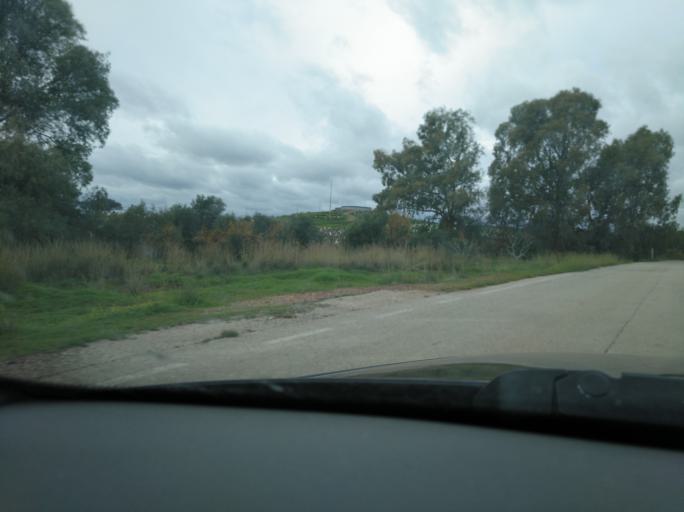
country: PT
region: Faro
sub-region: Vila Real de Santo Antonio
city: Monte Gordo
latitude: 37.2011
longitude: -7.4855
